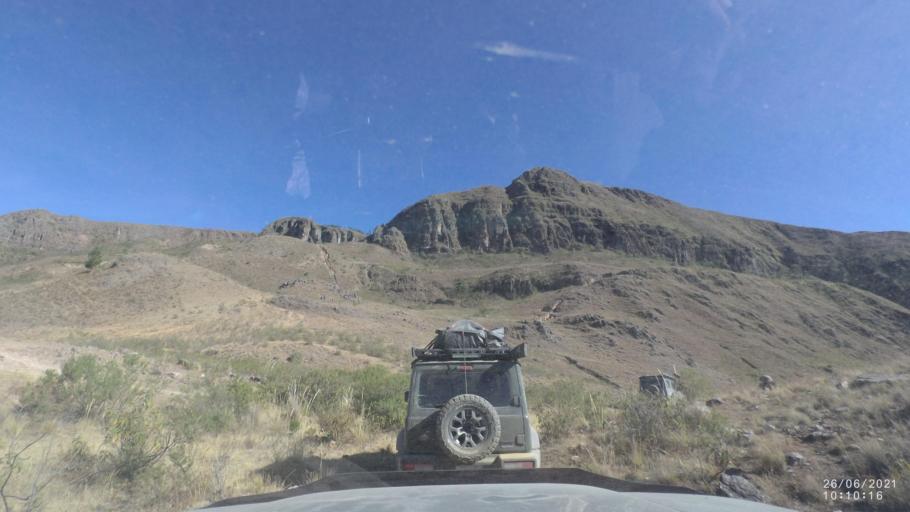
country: BO
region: Cochabamba
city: Mizque
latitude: -17.9178
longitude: -65.6252
